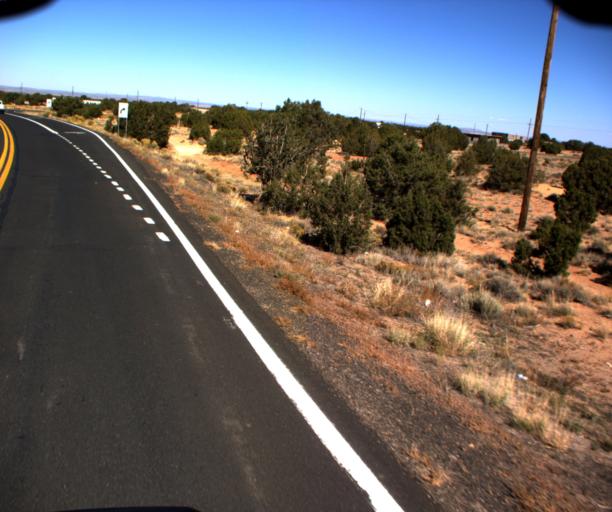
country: US
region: Arizona
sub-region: Navajo County
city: First Mesa
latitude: 35.8393
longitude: -110.5266
